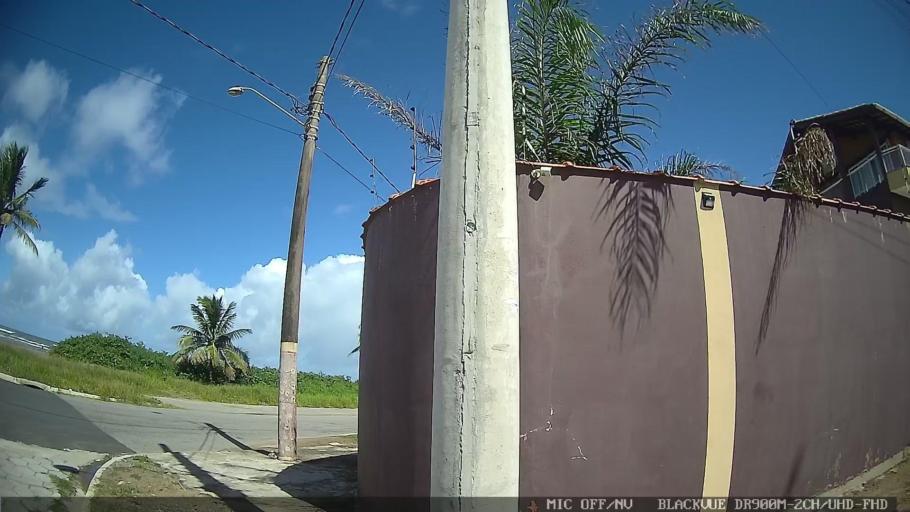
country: BR
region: Sao Paulo
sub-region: Itanhaem
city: Itanhaem
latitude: -24.2294
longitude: -46.8703
